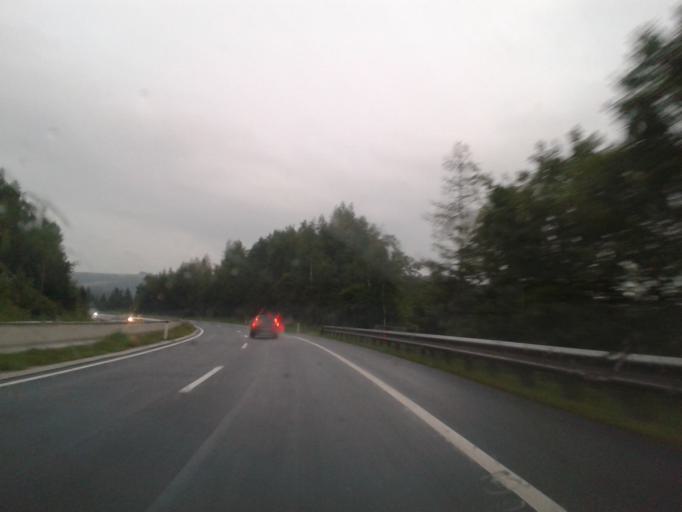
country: AT
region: Styria
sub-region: Politischer Bezirk Hartberg-Fuerstenfeld
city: Pinggau
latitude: 47.4316
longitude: 16.0993
